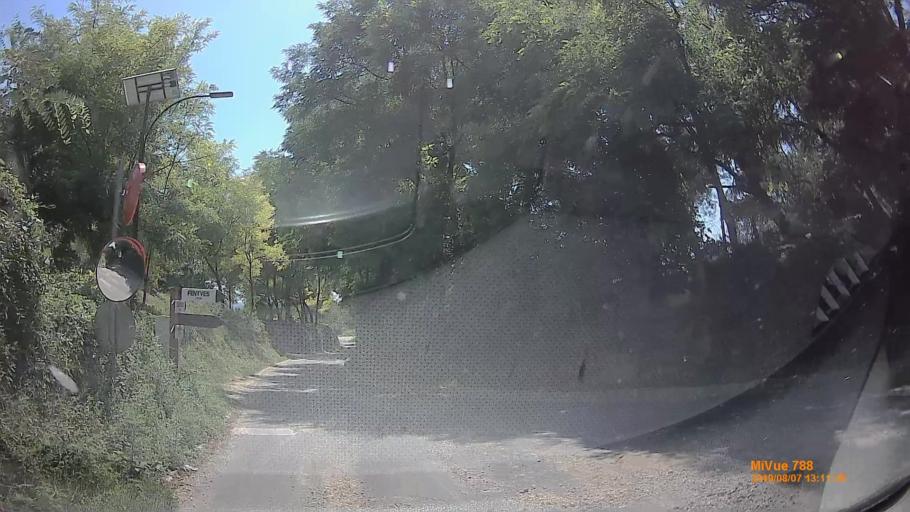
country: HU
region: Zala
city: Cserszegtomaj
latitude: 46.8081
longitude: 17.2231
